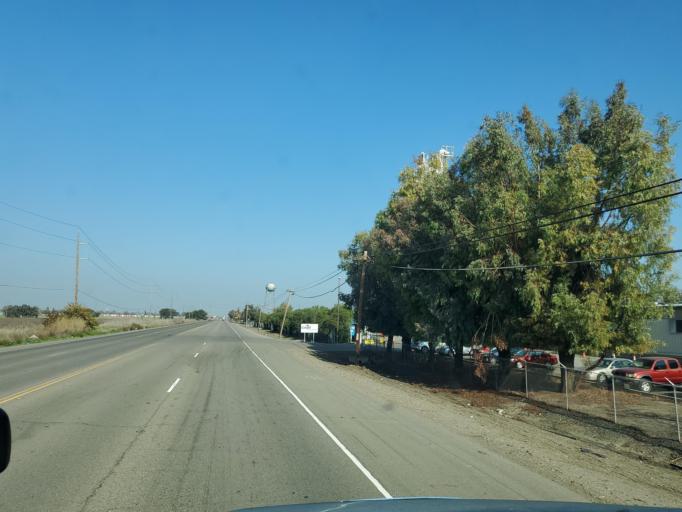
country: US
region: California
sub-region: San Joaquin County
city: French Camp
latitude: 37.8994
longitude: -121.2757
